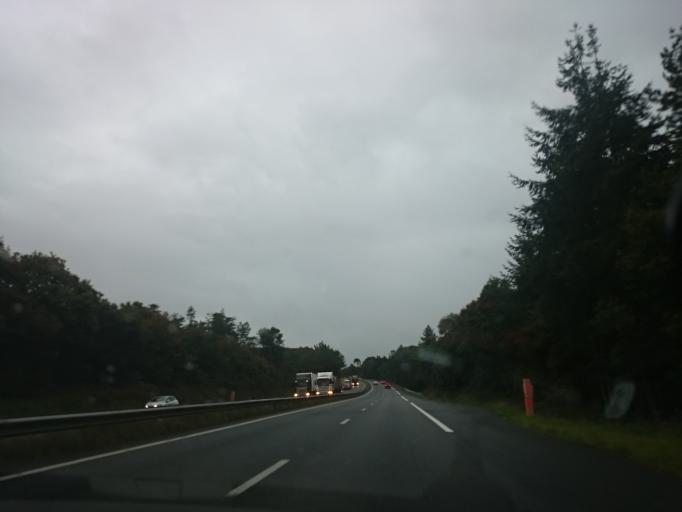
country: FR
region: Brittany
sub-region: Departement du Finistere
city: Hopital-Camfrout
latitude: 48.3356
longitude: -4.2295
